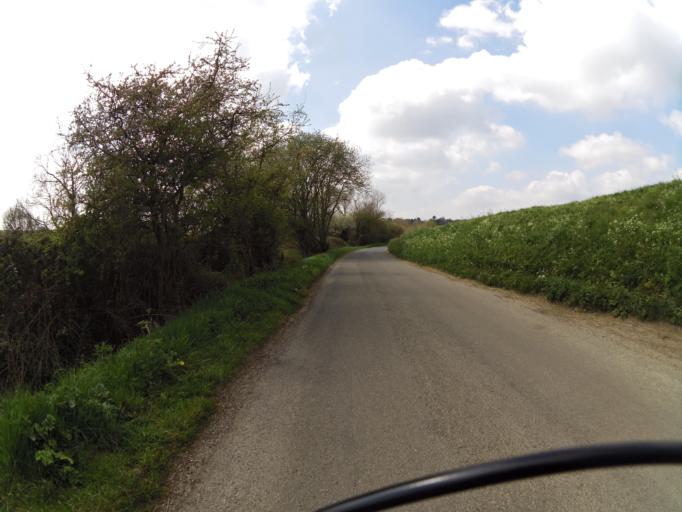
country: GB
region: England
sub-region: Suffolk
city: Hadleigh
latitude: 52.0625
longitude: 0.9244
